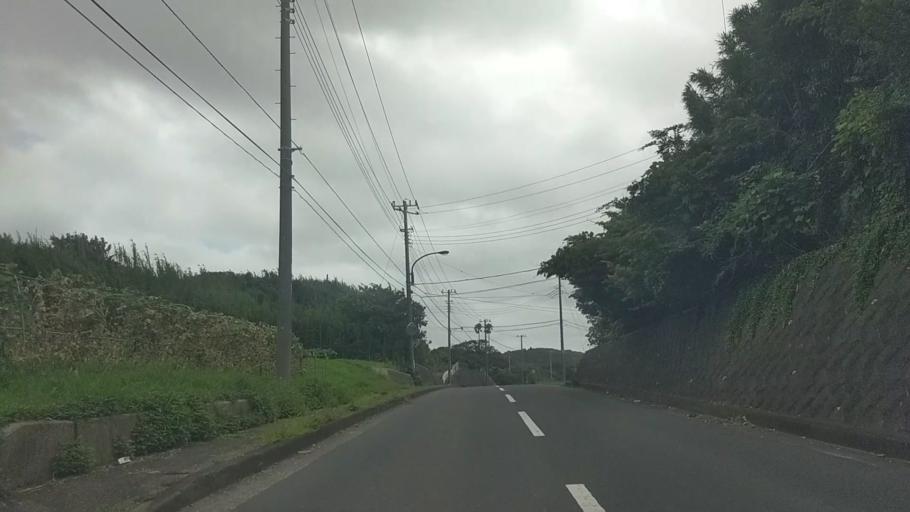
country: JP
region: Kanagawa
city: Hayama
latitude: 35.2331
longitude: 139.6256
